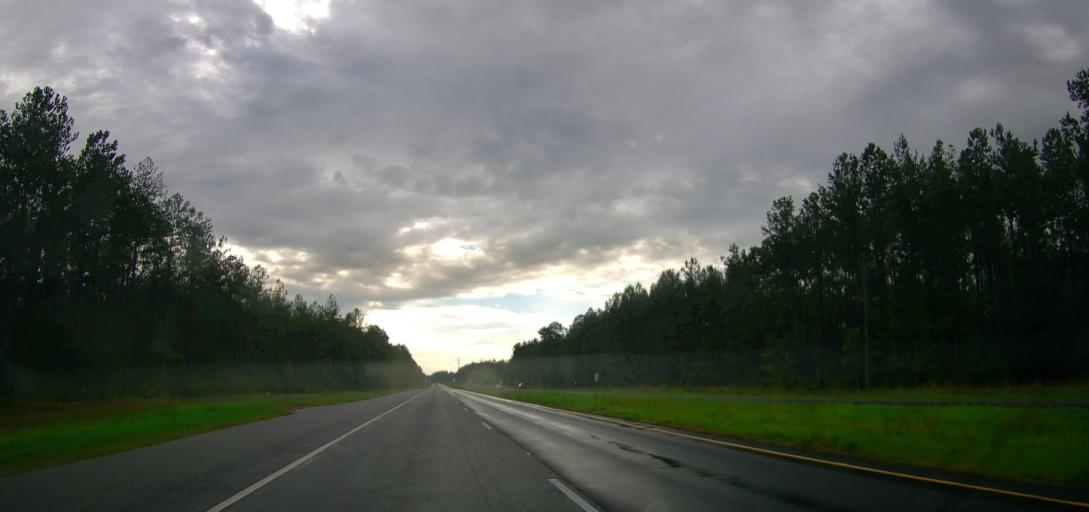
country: US
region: Georgia
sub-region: Ware County
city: Deenwood
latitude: 31.2608
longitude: -82.5124
